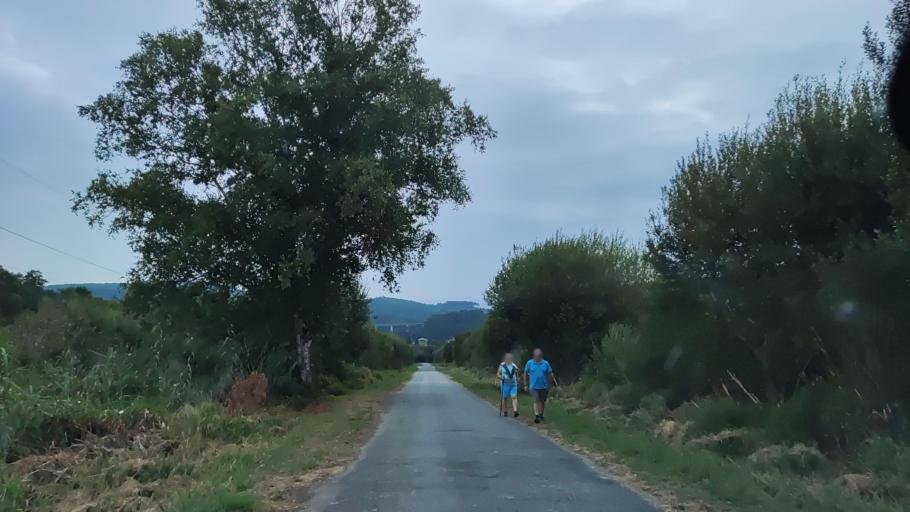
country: ES
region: Galicia
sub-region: Provincia da Coruna
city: Rois
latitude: 42.7150
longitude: -8.7105
